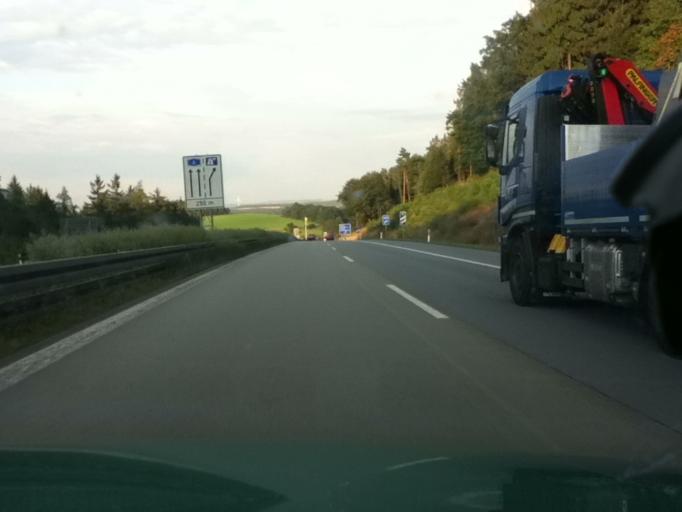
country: DE
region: Saxony
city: Rammenau
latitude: 51.1742
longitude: 14.1312
